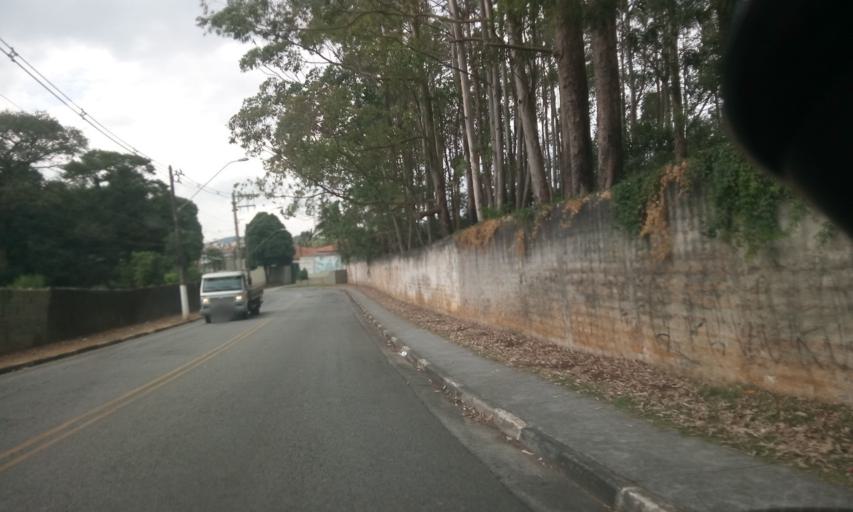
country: BR
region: Sao Paulo
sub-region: Sao Bernardo Do Campo
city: Sao Bernardo do Campo
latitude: -23.7738
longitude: -46.6050
